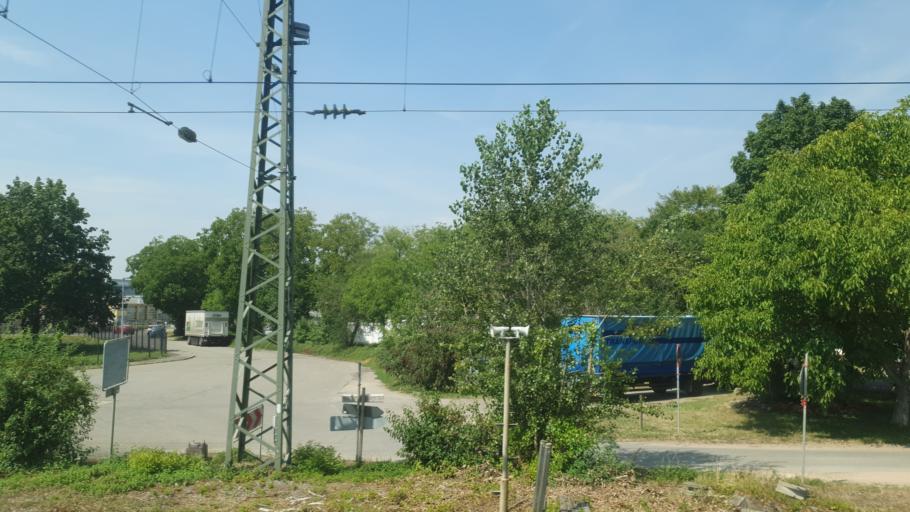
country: DE
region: Baden-Wuerttemberg
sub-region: Freiburg Region
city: Mullheim
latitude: 47.8133
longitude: 7.6016
